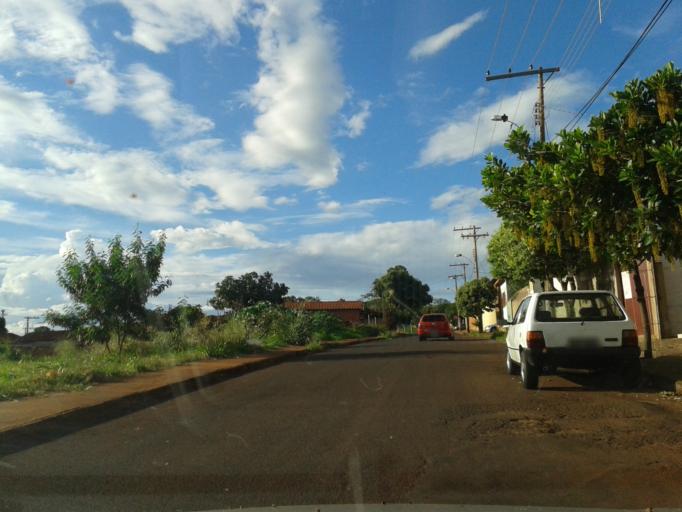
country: BR
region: Minas Gerais
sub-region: Ituiutaba
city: Ituiutaba
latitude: -18.9764
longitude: -49.4457
